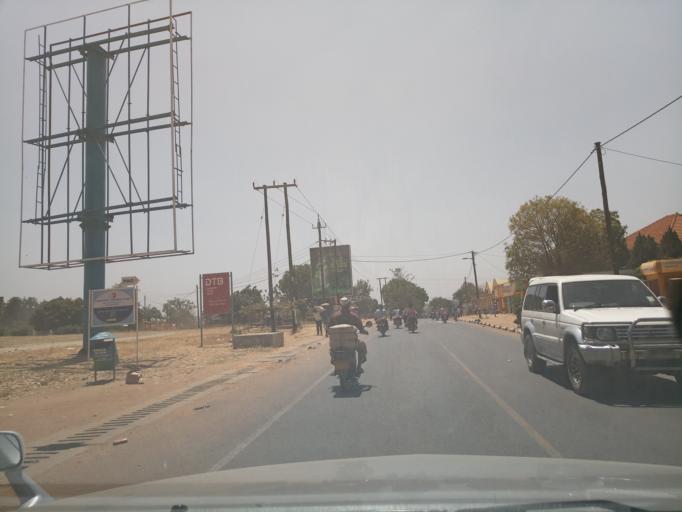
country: UG
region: Northern Region
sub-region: Arua District
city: Arua
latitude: 3.0130
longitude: 30.9139
